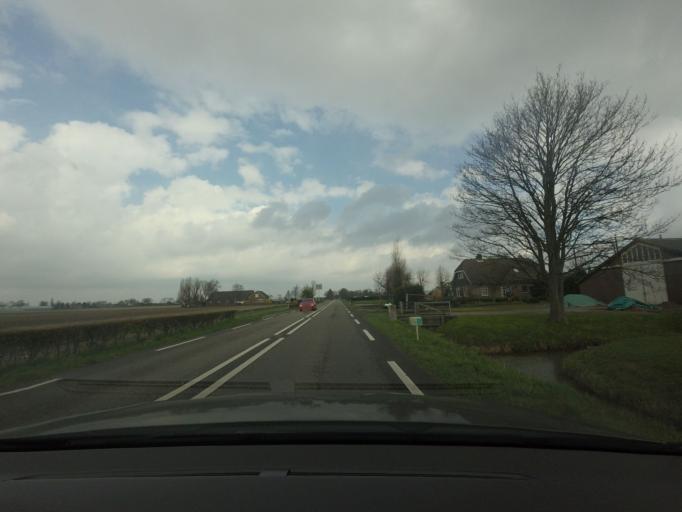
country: NL
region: South Holland
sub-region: Gemeente Nieuwkoop
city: Nieuwkoop
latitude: 52.2029
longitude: 4.7827
